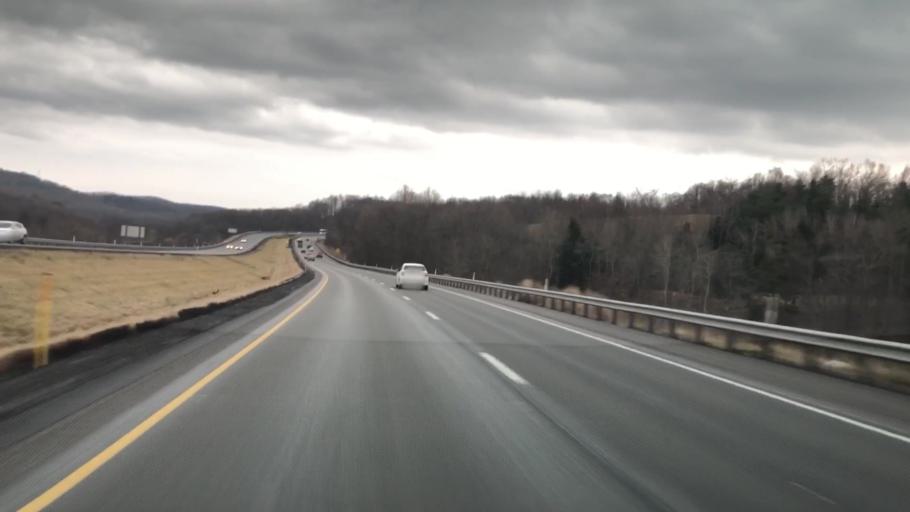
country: US
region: Pennsylvania
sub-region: Butler County
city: Prospect
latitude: 40.9114
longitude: -80.1289
